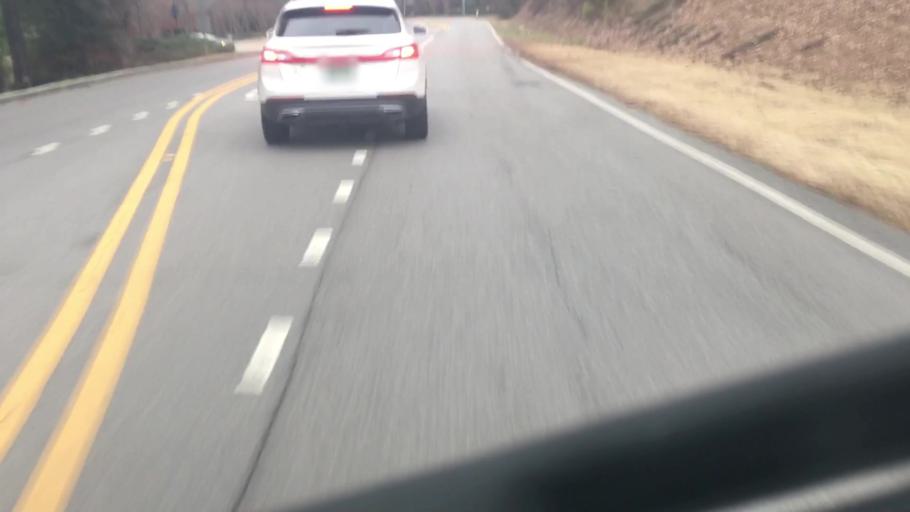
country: US
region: Alabama
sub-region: Jefferson County
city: Hoover
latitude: 33.3730
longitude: -86.8063
